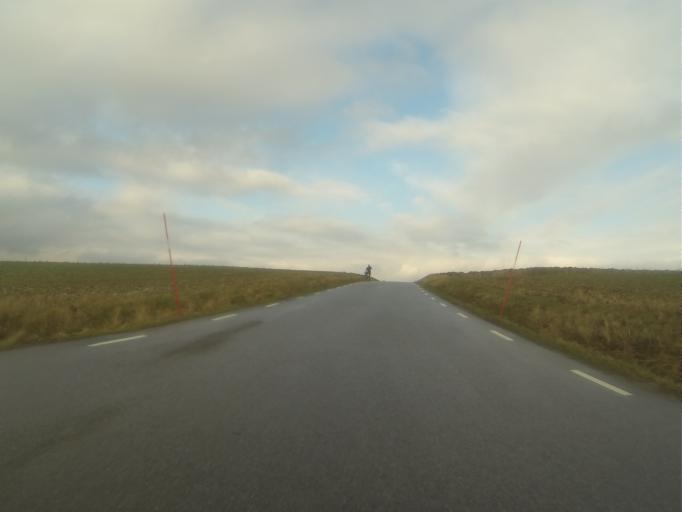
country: SE
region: Skane
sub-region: Svedala Kommun
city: Klagerup
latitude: 55.6152
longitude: 13.3077
